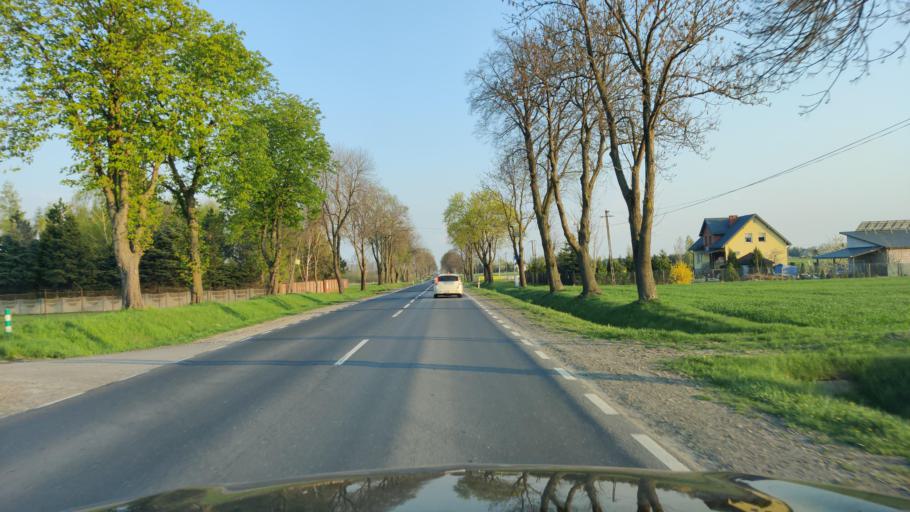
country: PL
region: Masovian Voivodeship
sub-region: Powiat pultuski
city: Pultusk
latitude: 52.6264
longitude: 21.0992
